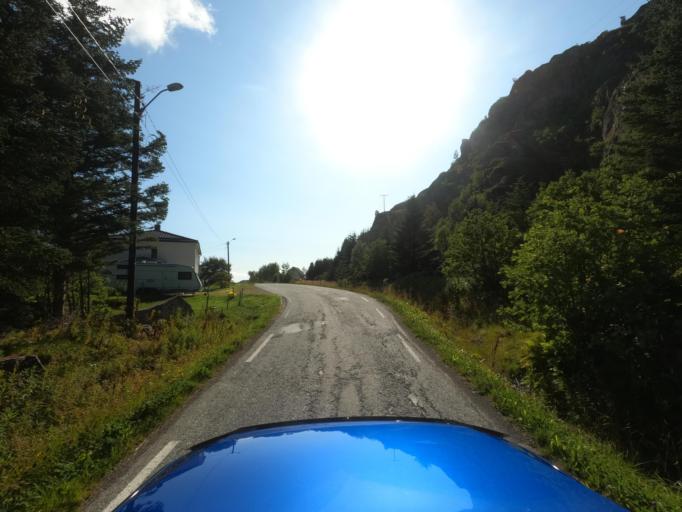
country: NO
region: Nordland
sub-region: Vestvagoy
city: Leknes
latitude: 68.1058
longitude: 13.7288
